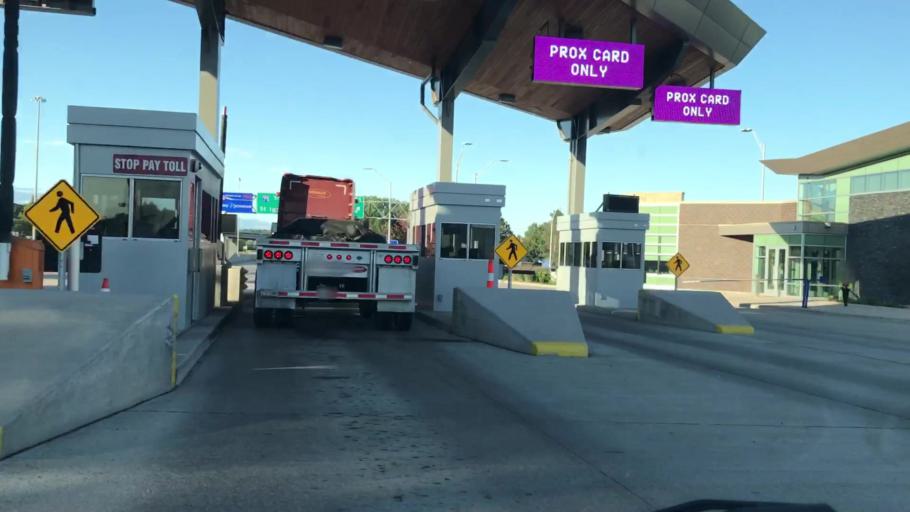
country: US
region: Michigan
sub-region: Chippewa County
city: Sault Ste. Marie
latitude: 46.4937
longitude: -84.3687
